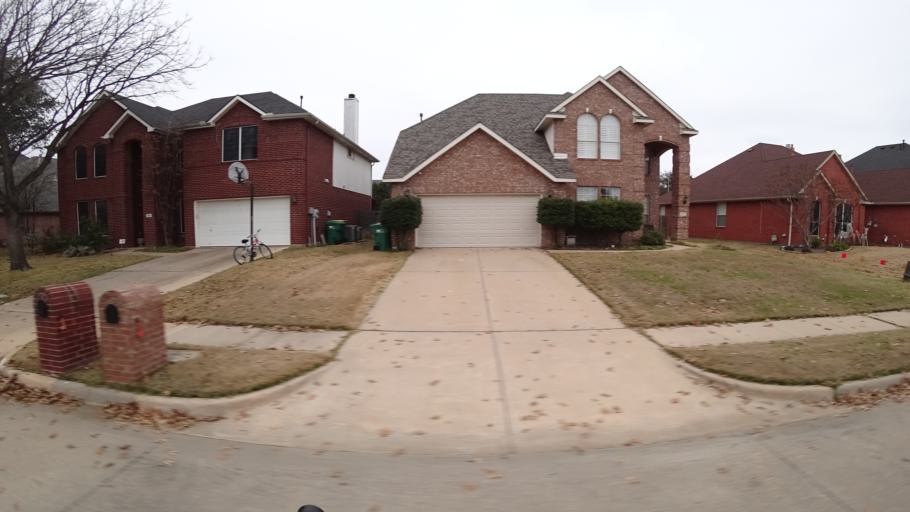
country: US
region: Texas
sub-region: Denton County
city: Lewisville
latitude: 33.0564
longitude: -97.0261
